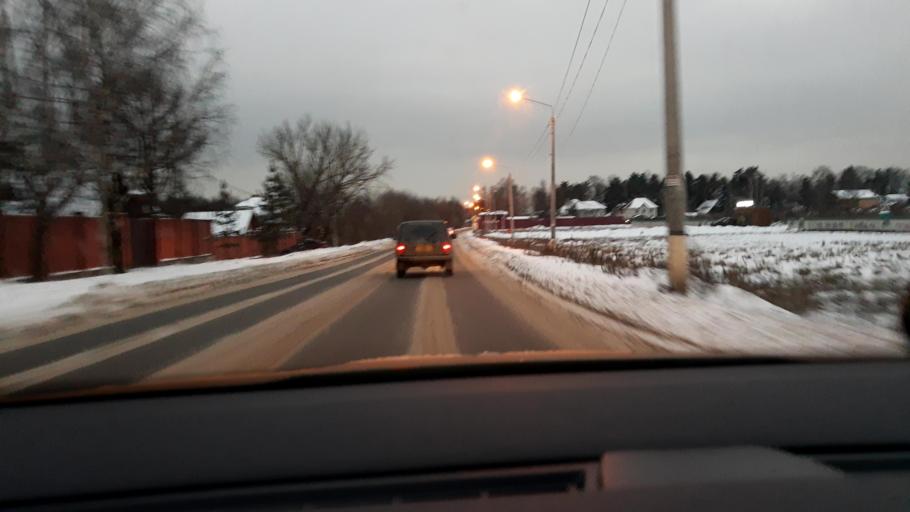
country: RU
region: Moskovskaya
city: Tomilino
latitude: 55.6469
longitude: 37.9546
